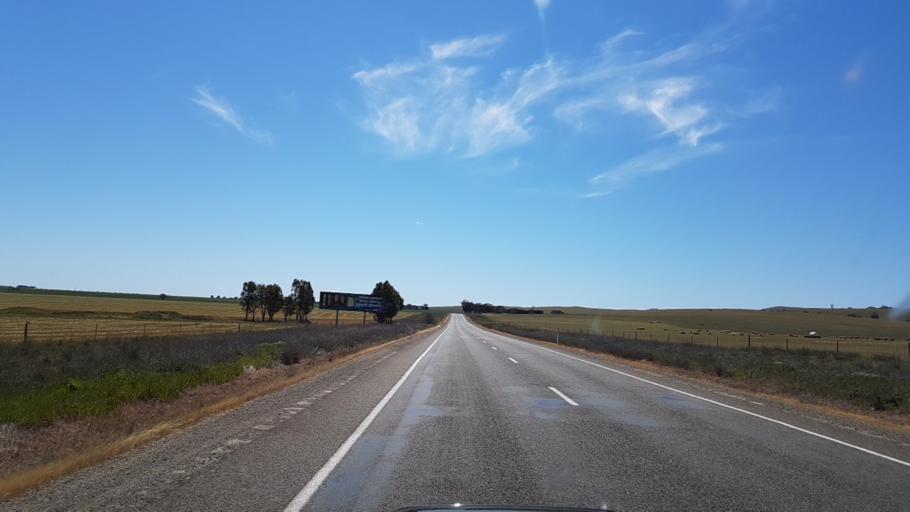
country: AU
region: South Australia
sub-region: Northern Areas
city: Jamestown
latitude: -33.4583
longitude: 138.8916
